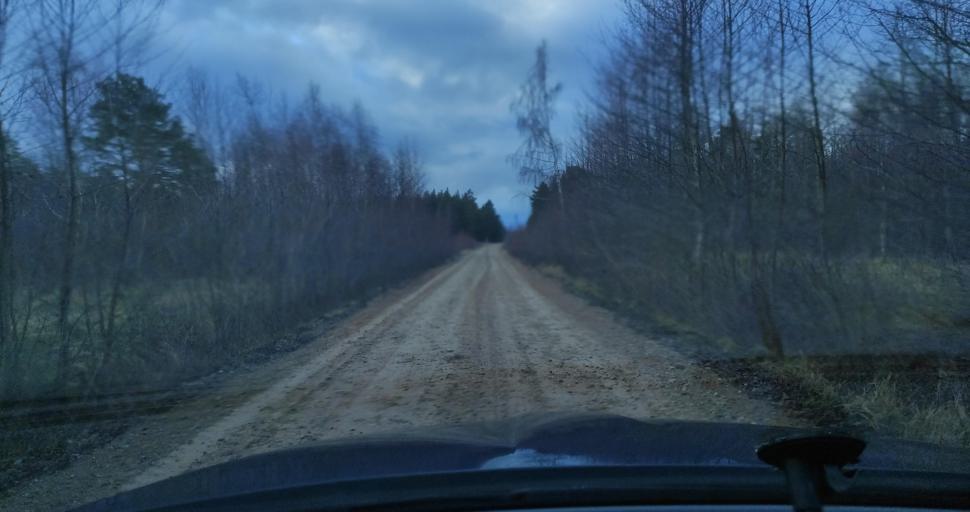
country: LV
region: Pavilostas
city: Pavilosta
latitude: 56.8147
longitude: 21.0649
